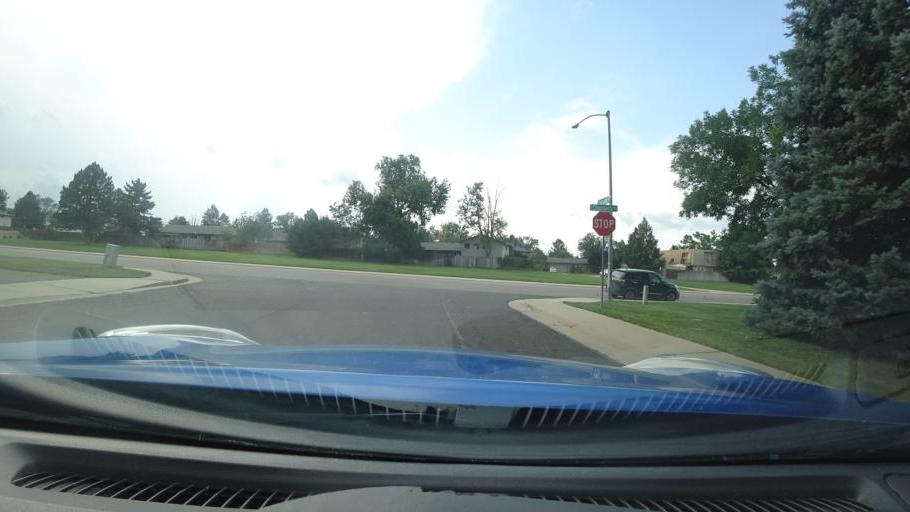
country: US
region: Colorado
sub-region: Adams County
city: Aurora
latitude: 39.6939
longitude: -104.8134
